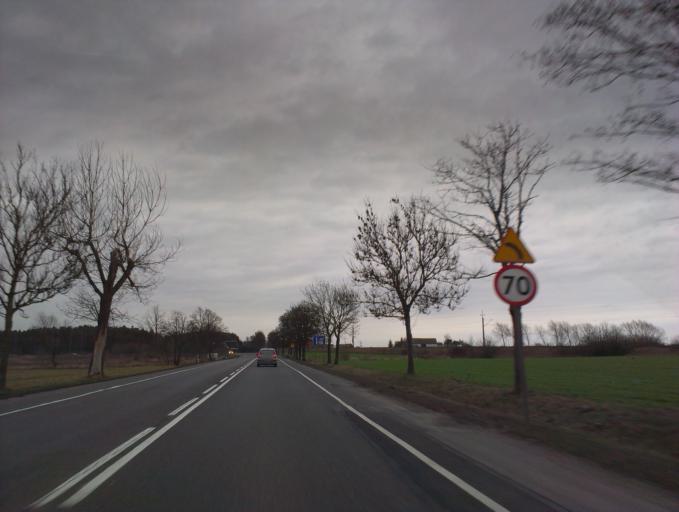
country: PL
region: Greater Poland Voivodeship
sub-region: Powiat obornicki
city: Oborniki
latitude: 52.6915
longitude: 16.8894
